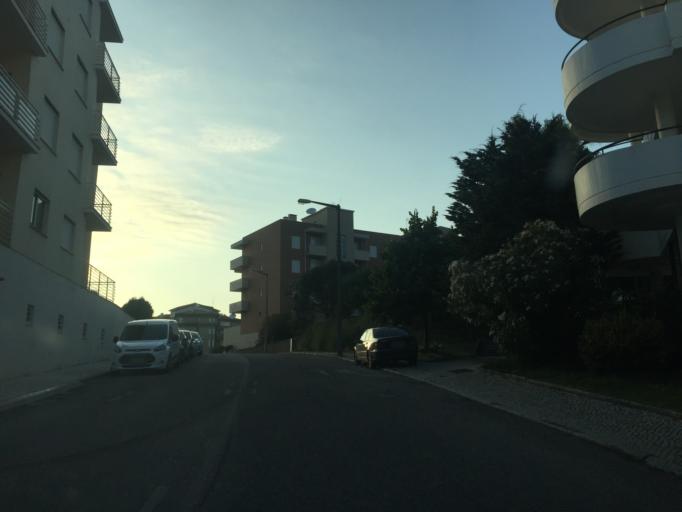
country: PT
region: Coimbra
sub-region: Figueira da Foz
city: Figueira da Foz
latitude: 40.1600
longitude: -8.8664
